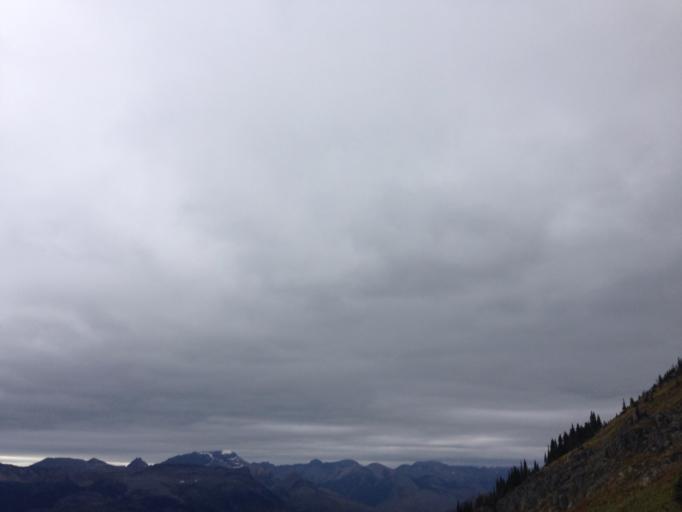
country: US
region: Montana
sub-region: Flathead County
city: Columbia Falls
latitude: 48.7450
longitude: -113.7398
